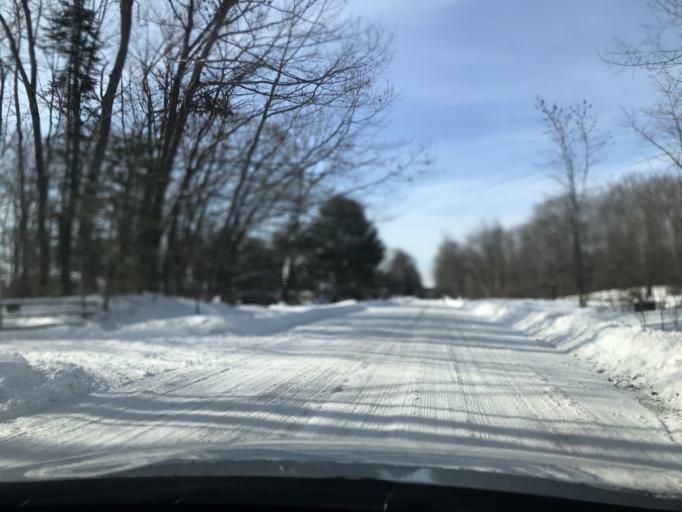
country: US
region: Wisconsin
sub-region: Oconto County
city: Gillett
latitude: 45.1570
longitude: -88.1992
